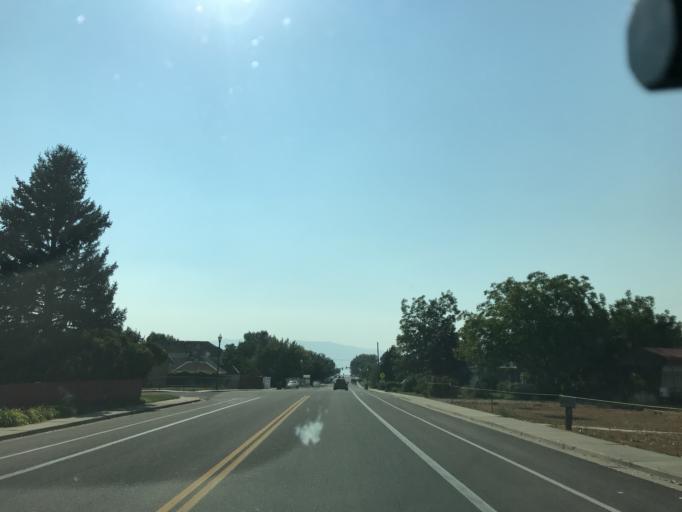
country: US
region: Utah
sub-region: Utah County
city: Orem
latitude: 40.2824
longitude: -111.7006
